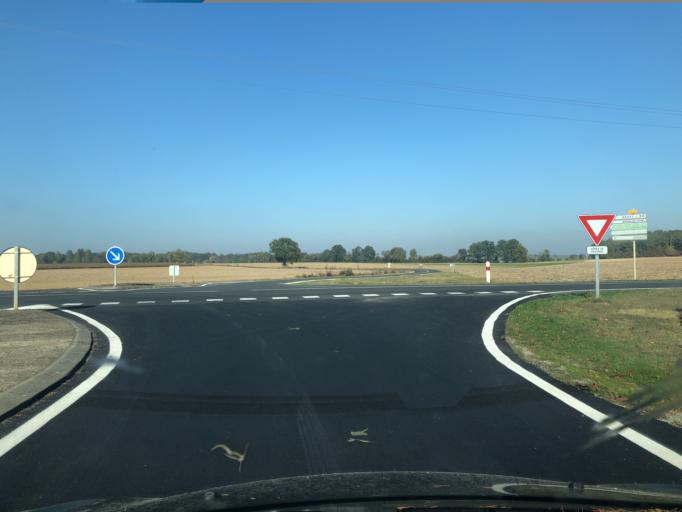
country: FR
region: Centre
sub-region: Departement d'Indre-et-Loire
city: Neuvy-le-Roi
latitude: 47.5604
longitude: 0.6110
